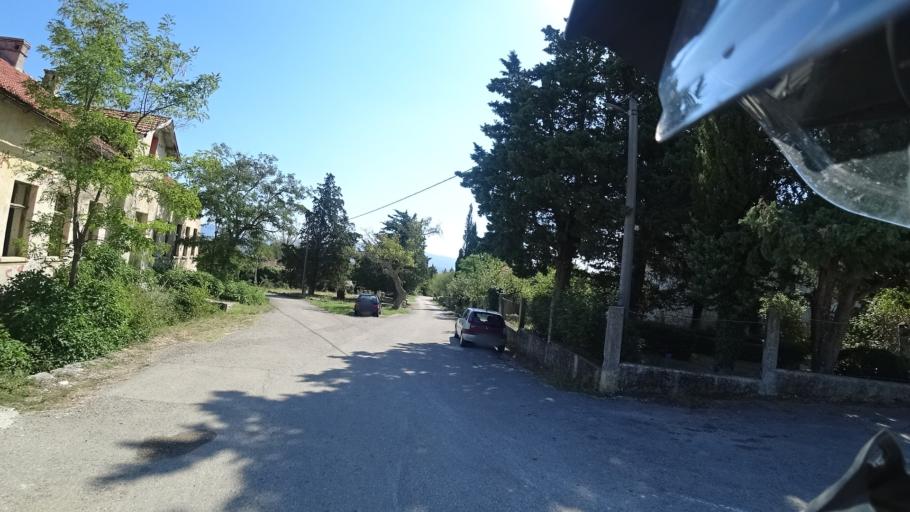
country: HR
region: Sibensko-Kniniska
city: Drnis
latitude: 43.8781
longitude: 16.1929
